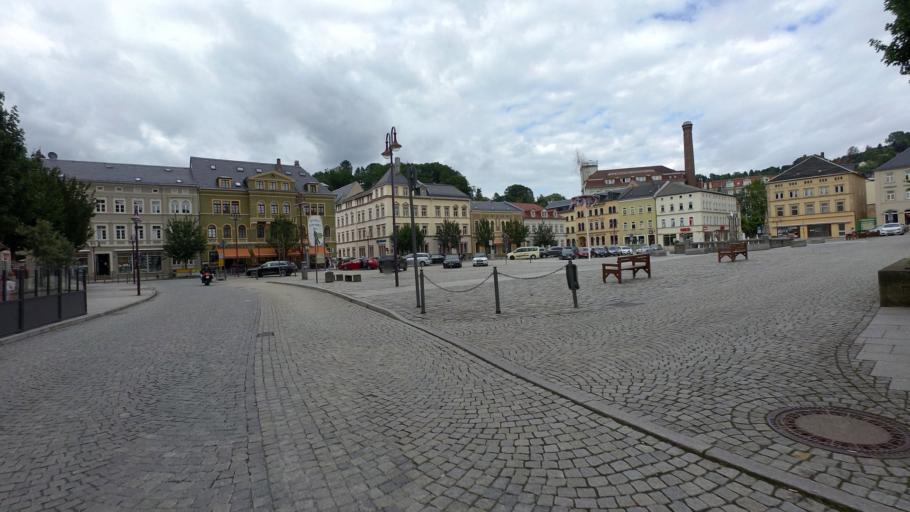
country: DE
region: Saxony
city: Sebnitz
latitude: 50.9724
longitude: 14.2711
